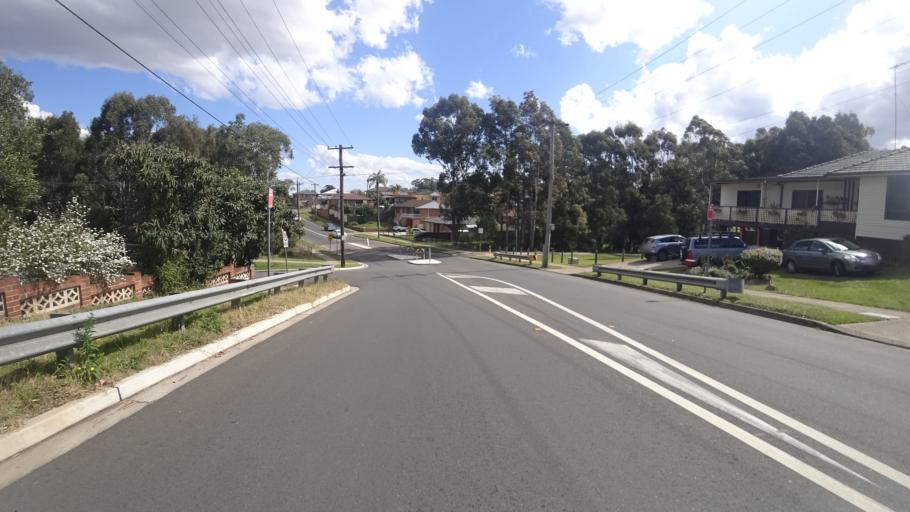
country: AU
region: New South Wales
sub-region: Fairfield
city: Cabramatta West
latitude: -33.9062
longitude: 150.9087
